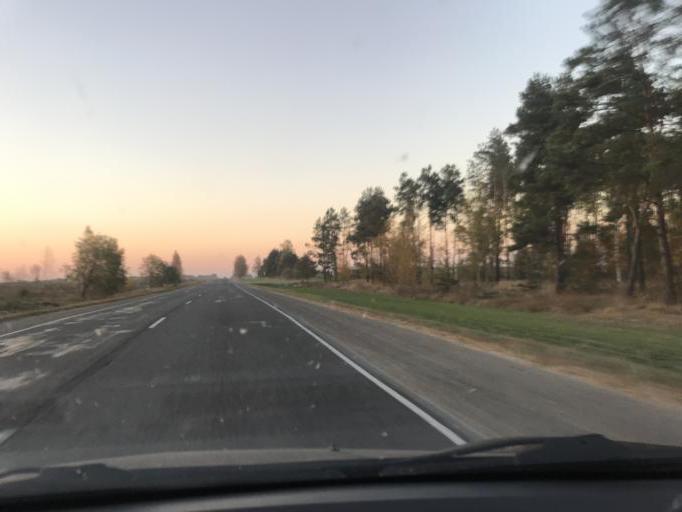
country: BY
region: Gomel
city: Horad Rechytsa
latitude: 52.1948
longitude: 30.5472
